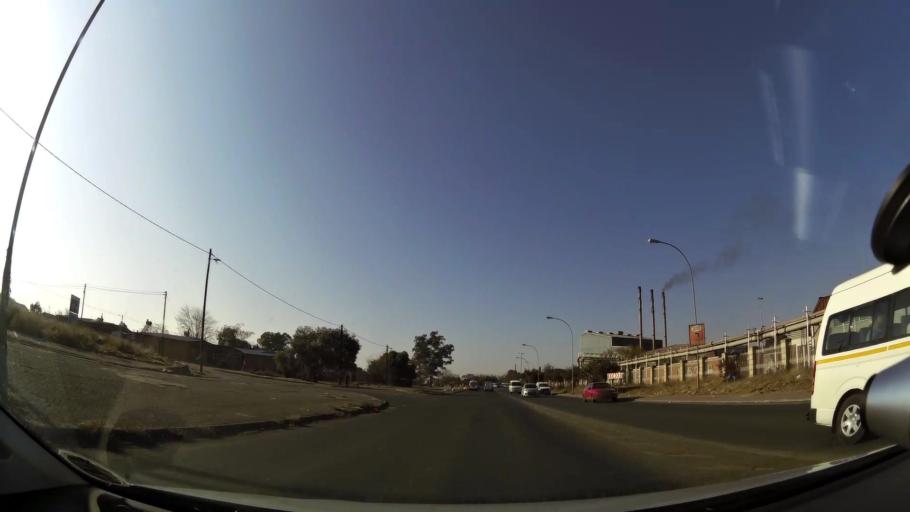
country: ZA
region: Orange Free State
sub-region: Mangaung Metropolitan Municipality
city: Bloemfontein
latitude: -29.1396
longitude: 26.2458
